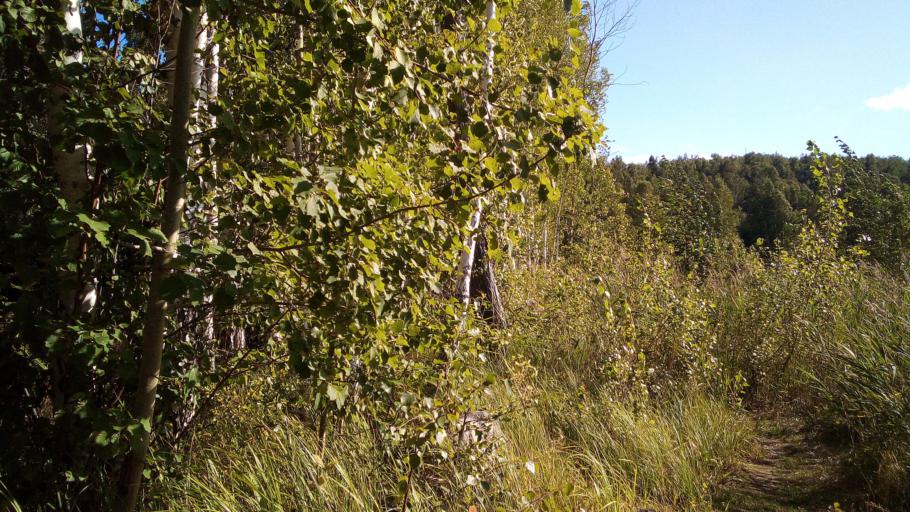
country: RU
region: Chelyabinsk
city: Tayginka
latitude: 55.4786
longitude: 60.4937
